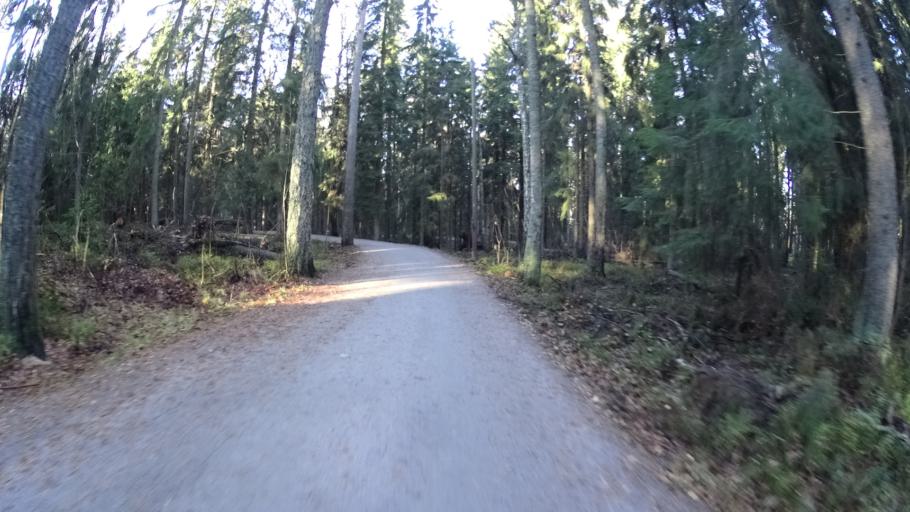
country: FI
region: Uusimaa
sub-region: Helsinki
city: Helsinki
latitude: 60.2253
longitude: 24.9184
